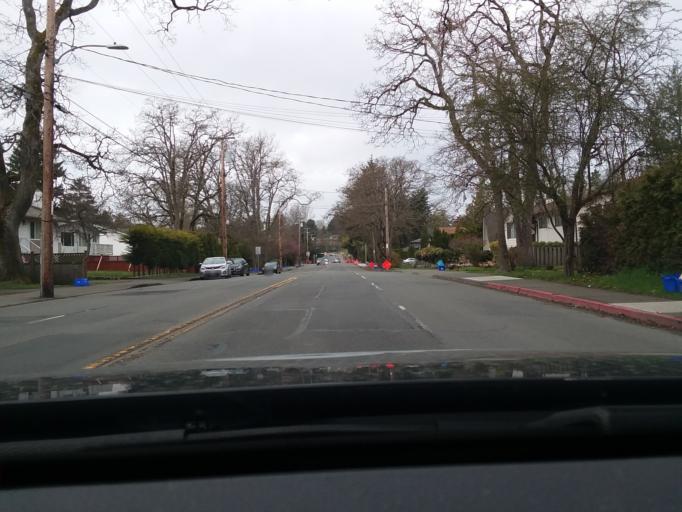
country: CA
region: British Columbia
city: Oak Bay
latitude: 48.4760
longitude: -123.3289
